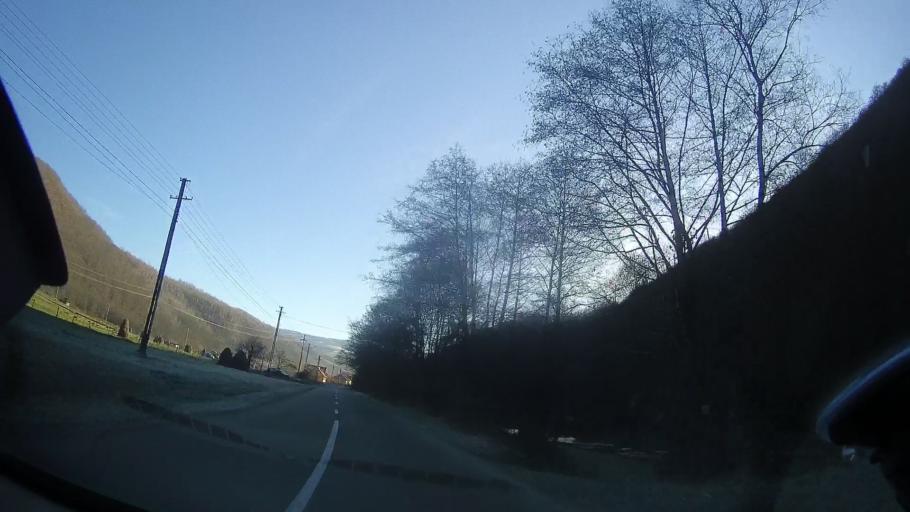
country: RO
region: Bihor
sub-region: Comuna Bulz
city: Bulz
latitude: 46.9100
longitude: 22.6770
